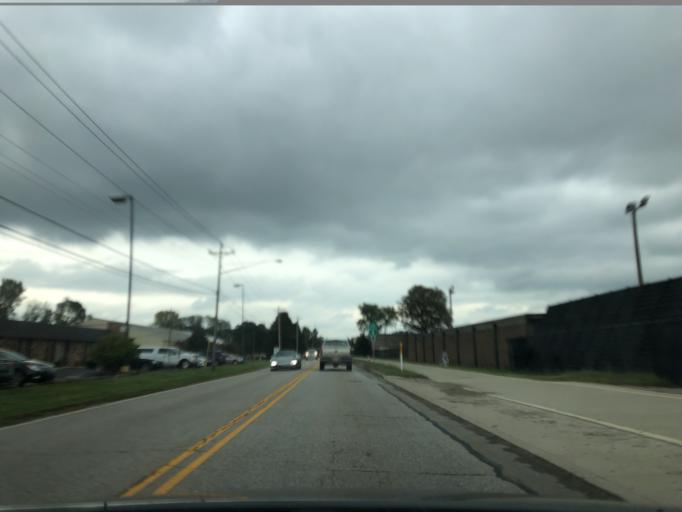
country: US
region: Ohio
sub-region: Hamilton County
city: Turpin Hills
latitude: 39.1111
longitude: -84.4198
